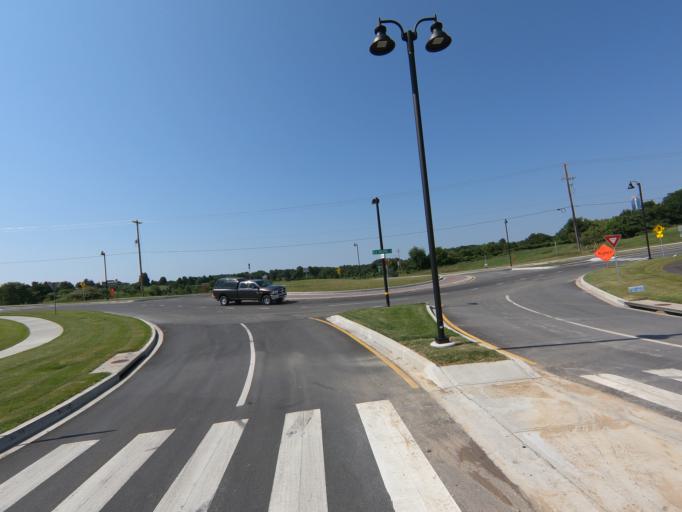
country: US
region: Maryland
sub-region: Frederick County
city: Spring Ridge
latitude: 39.3904
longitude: -77.3108
